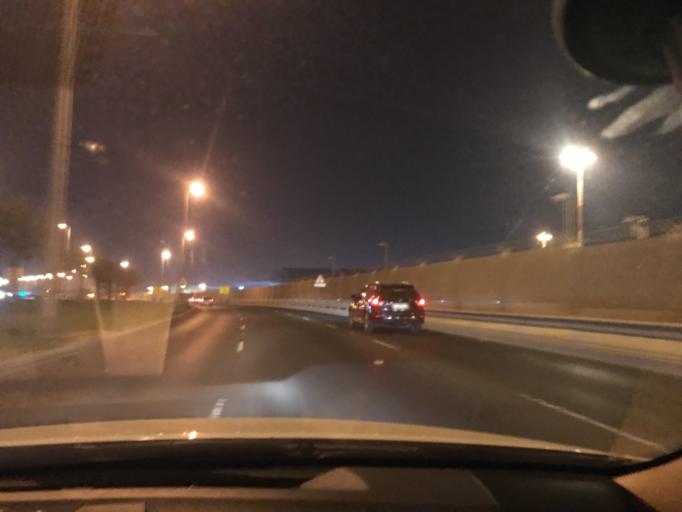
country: BH
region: Muharraq
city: Al Hadd
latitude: 26.2626
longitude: 50.6394
